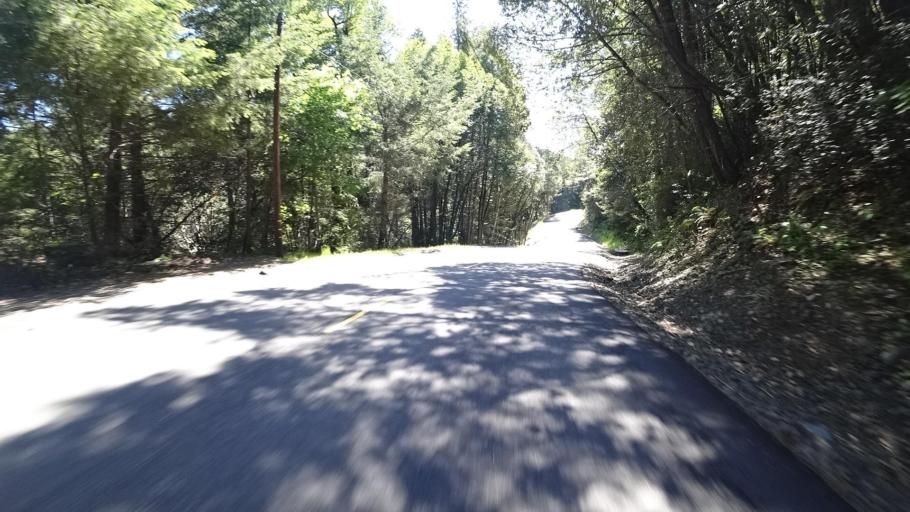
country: US
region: California
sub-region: Humboldt County
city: Rio Dell
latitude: 40.2706
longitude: -124.2068
